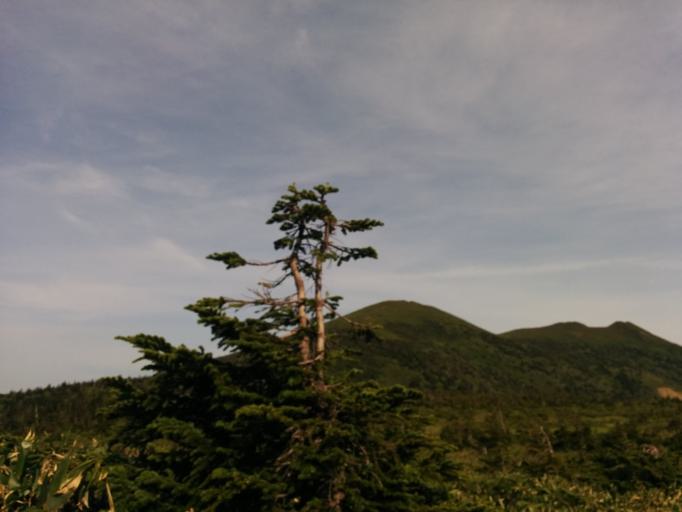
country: JP
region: Aomori
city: Aomori Shi
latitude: 40.6752
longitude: 140.8646
